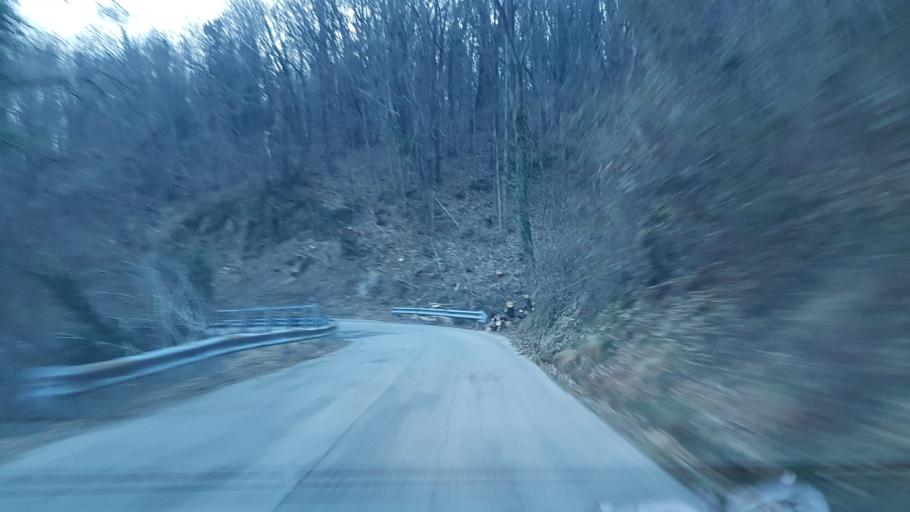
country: IT
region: Friuli Venezia Giulia
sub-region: Provincia di Udine
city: Attimis
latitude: 46.2024
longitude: 13.3380
